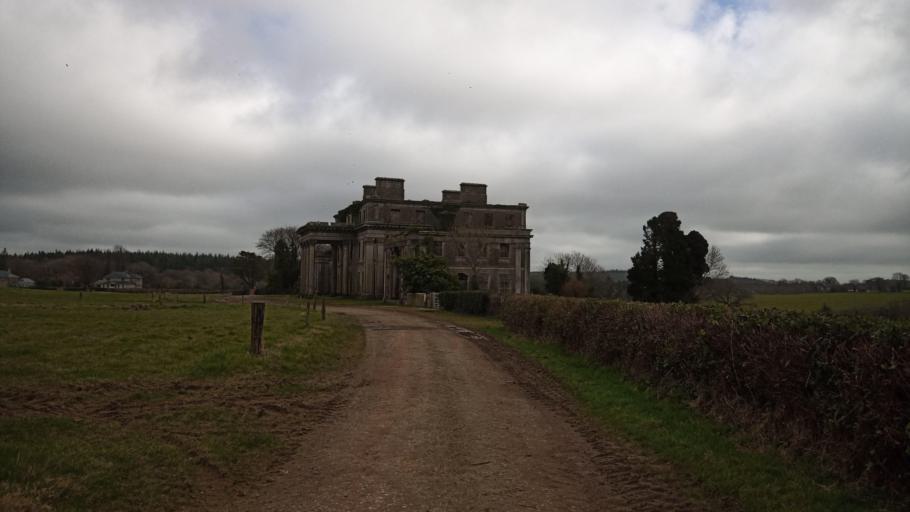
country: IE
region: Leinster
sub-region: Loch Garman
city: Enniscorthy
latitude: 52.4806
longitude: -6.7275
